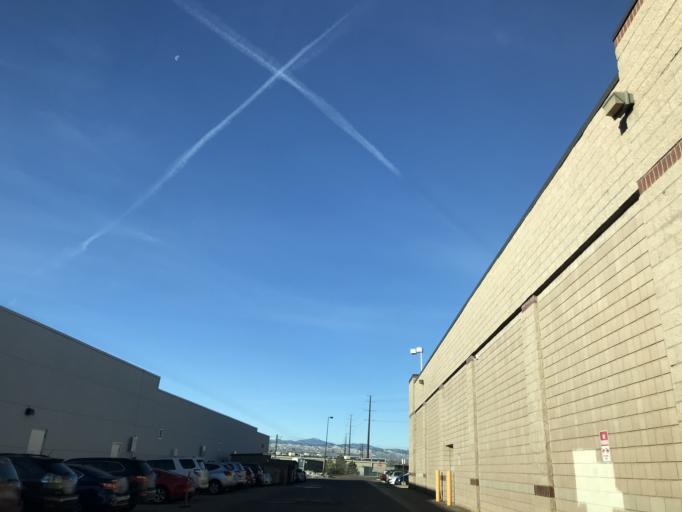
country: US
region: Colorado
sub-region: Denver County
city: Denver
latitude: 39.7076
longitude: -104.9906
